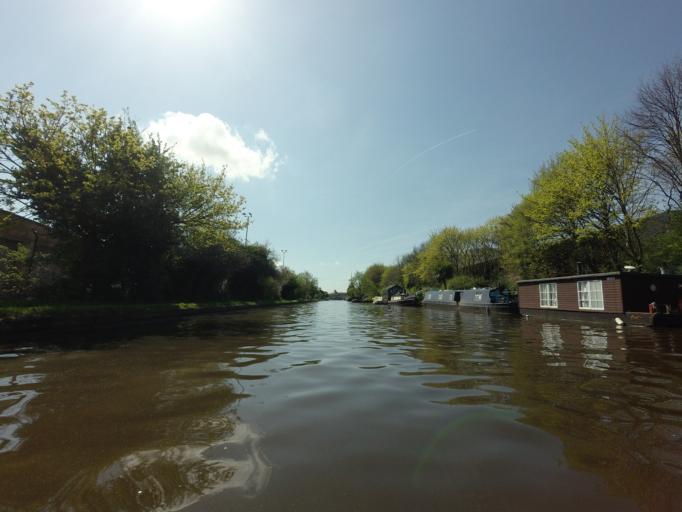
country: GB
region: England
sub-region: Greater London
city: Hayes
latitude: 51.5021
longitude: -0.4045
